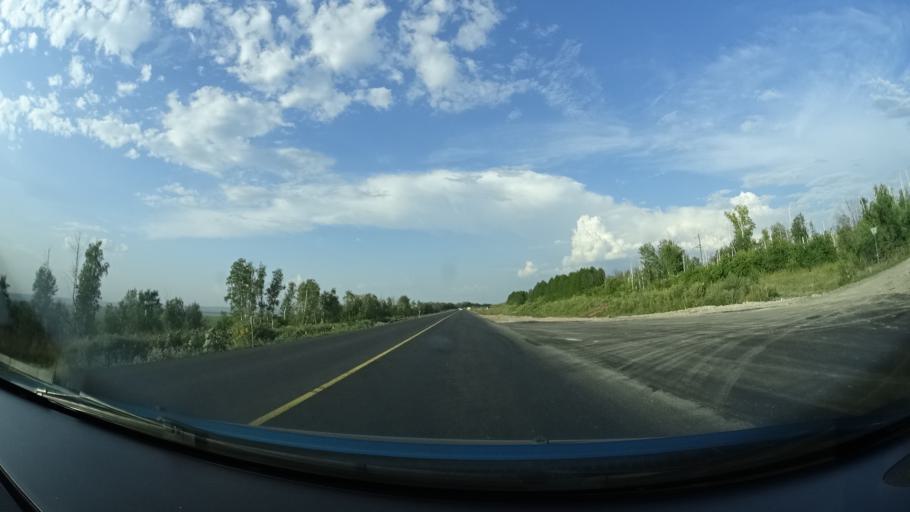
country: RU
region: Samara
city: Sukhodol
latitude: 53.7689
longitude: 50.8922
